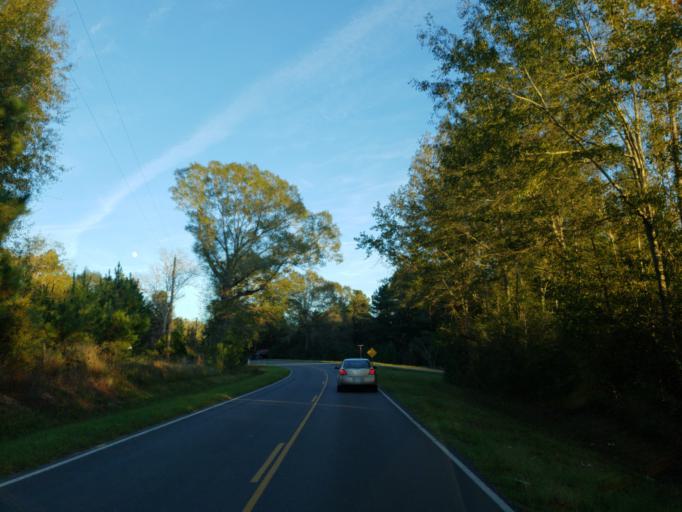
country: US
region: Mississippi
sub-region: Wayne County
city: Belmont
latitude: 31.4378
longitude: -88.4967
